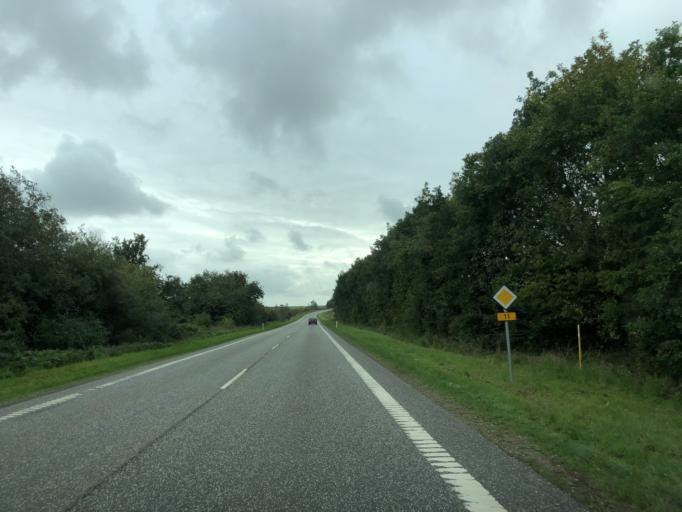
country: DK
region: North Denmark
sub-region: Thisted Kommune
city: Hurup
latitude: 56.7836
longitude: 8.4671
